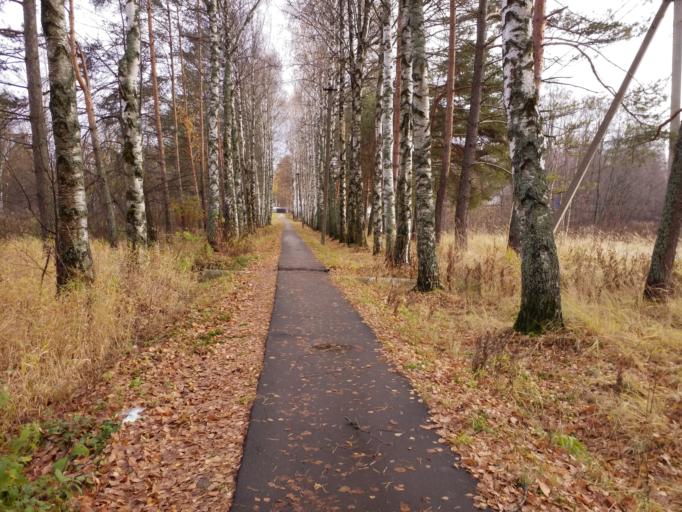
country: RU
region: Moskovskaya
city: Ashukino
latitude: 56.1632
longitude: 37.9423
